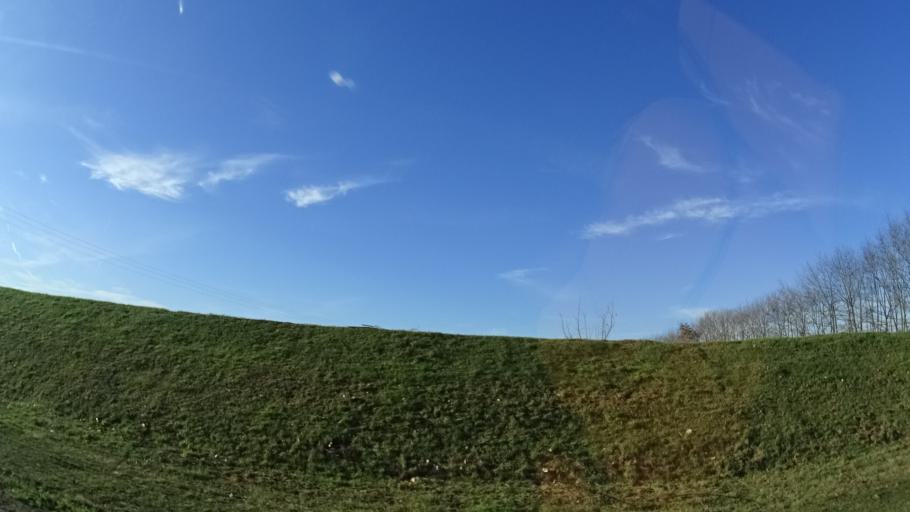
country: DE
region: Baden-Wuerttemberg
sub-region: Karlsruhe Region
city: Sankt Leon-Rot
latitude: 49.2669
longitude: 8.6441
